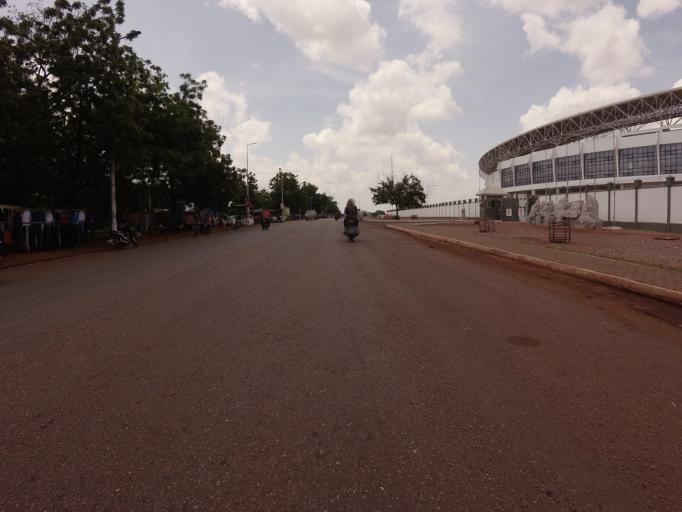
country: GH
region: Northern
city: Tamale
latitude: 9.4105
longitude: -0.8632
